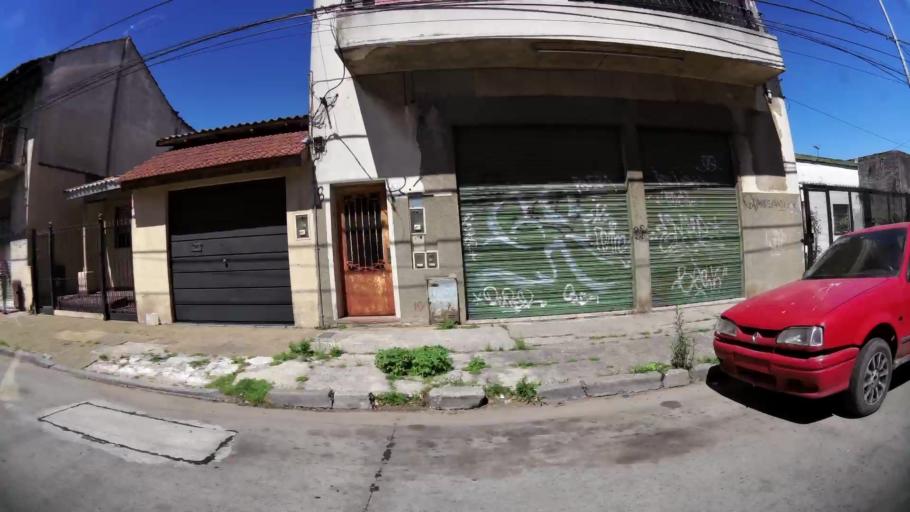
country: AR
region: Buenos Aires
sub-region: Partido de General San Martin
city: General San Martin
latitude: -34.5435
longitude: -58.5386
